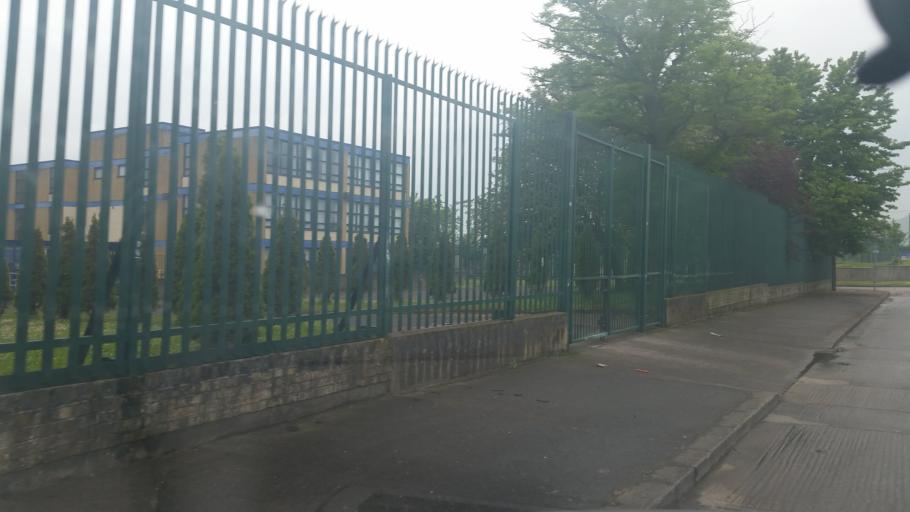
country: IE
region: Leinster
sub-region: Dublin City
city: Finglas
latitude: 53.3846
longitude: -6.3175
